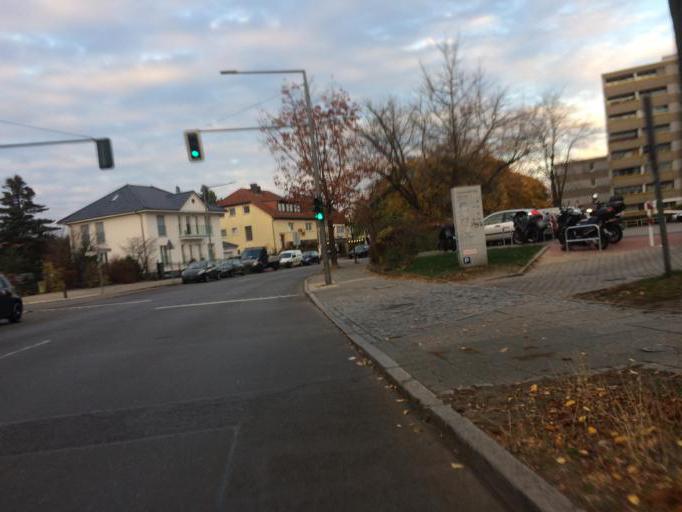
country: DE
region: Berlin
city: Markisches Viertel
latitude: 52.5918
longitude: 13.3482
